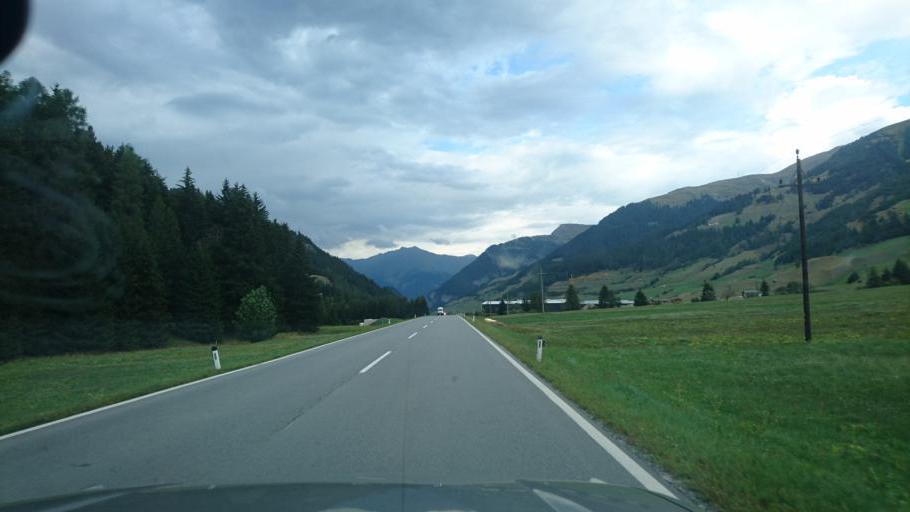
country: AT
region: Tyrol
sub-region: Politischer Bezirk Landeck
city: Nauders
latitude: 46.8692
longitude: 10.5087
